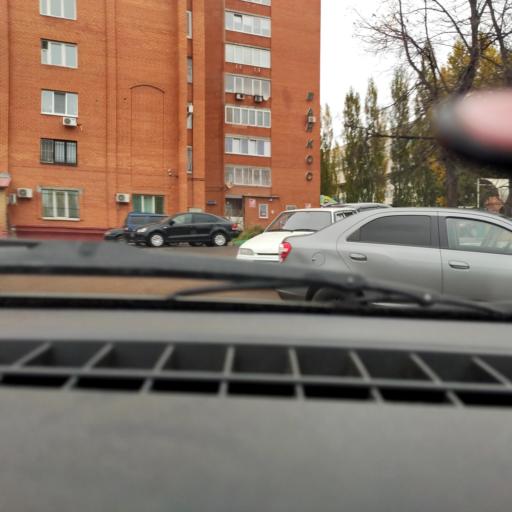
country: RU
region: Bashkortostan
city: Ufa
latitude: 54.7159
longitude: 56.0127
